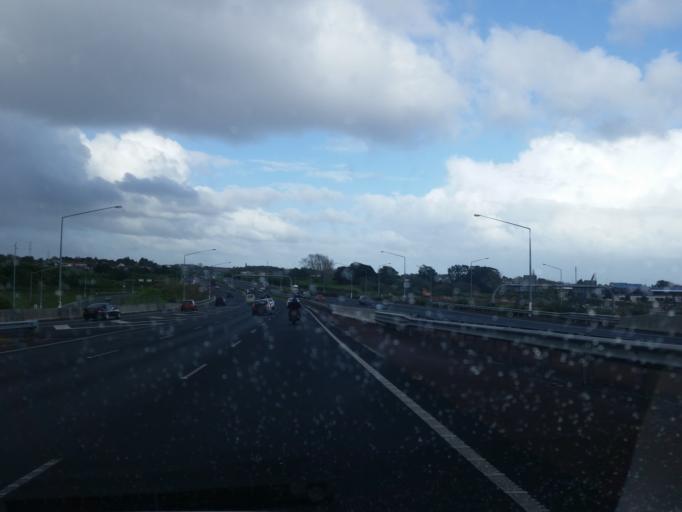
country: NZ
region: Auckland
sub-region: Auckland
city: Manukau City
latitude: -36.9961
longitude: 174.8899
